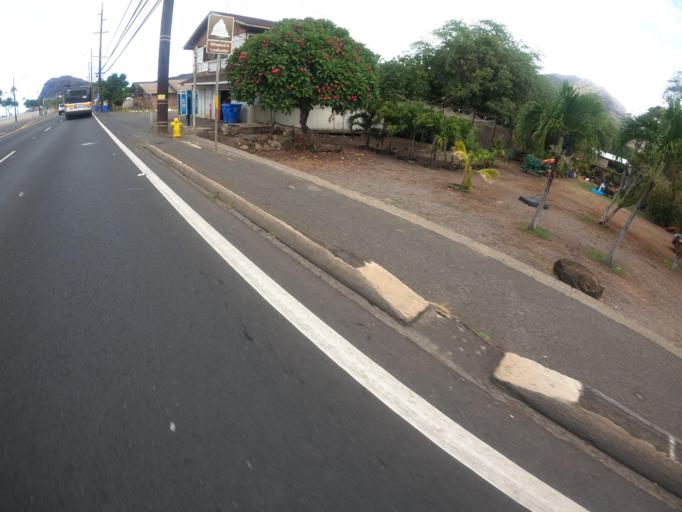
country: US
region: Hawaii
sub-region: Honolulu County
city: Nanakuli
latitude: 21.3835
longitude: -158.1475
